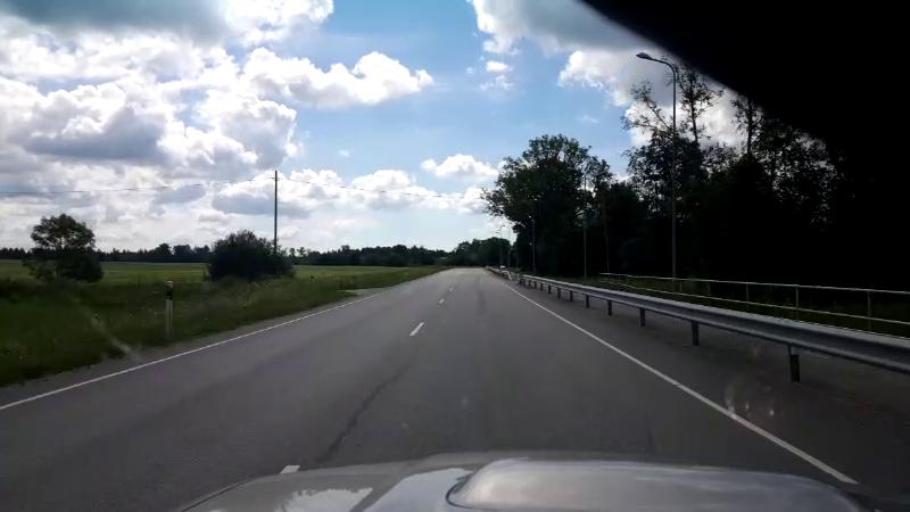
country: EE
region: Jaervamaa
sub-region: Jaerva-Jaani vald
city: Jarva-Jaani
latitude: 59.0253
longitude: 25.7045
